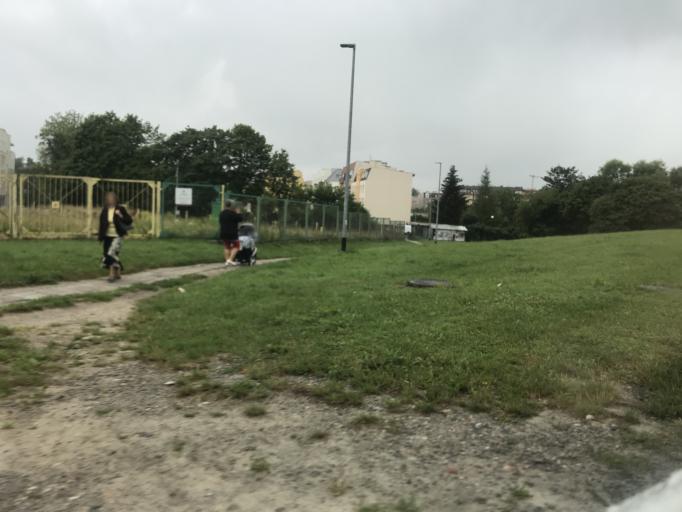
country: PL
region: Warmian-Masurian Voivodeship
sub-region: Powiat elblaski
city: Elblag
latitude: 54.1613
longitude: 19.4176
